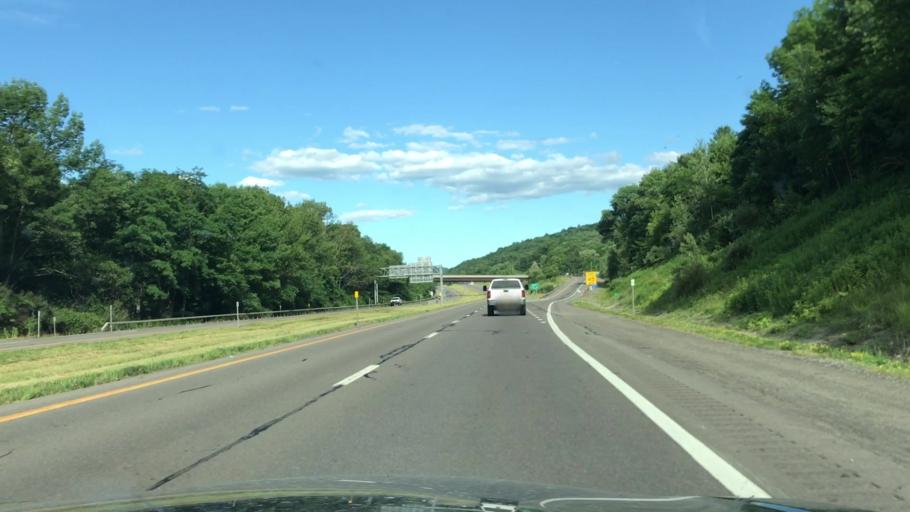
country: US
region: New York
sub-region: Broome County
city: Chenango Bridge
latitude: 42.1008
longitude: -75.7997
